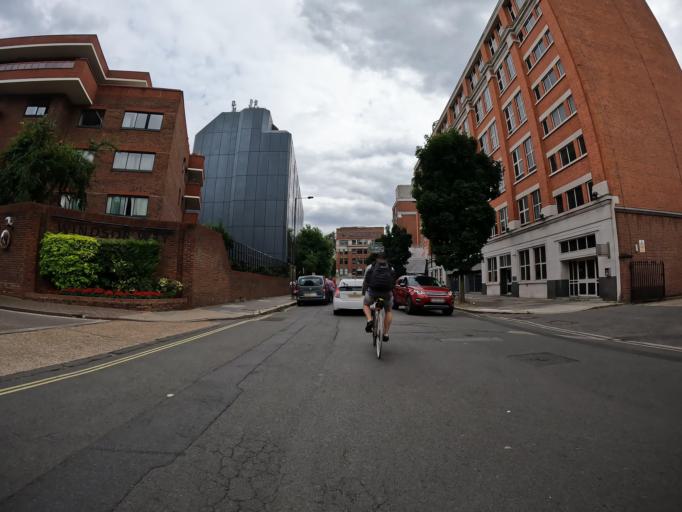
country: GB
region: England
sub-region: Greater London
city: Hammersmith
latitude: 51.4951
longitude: -0.2162
